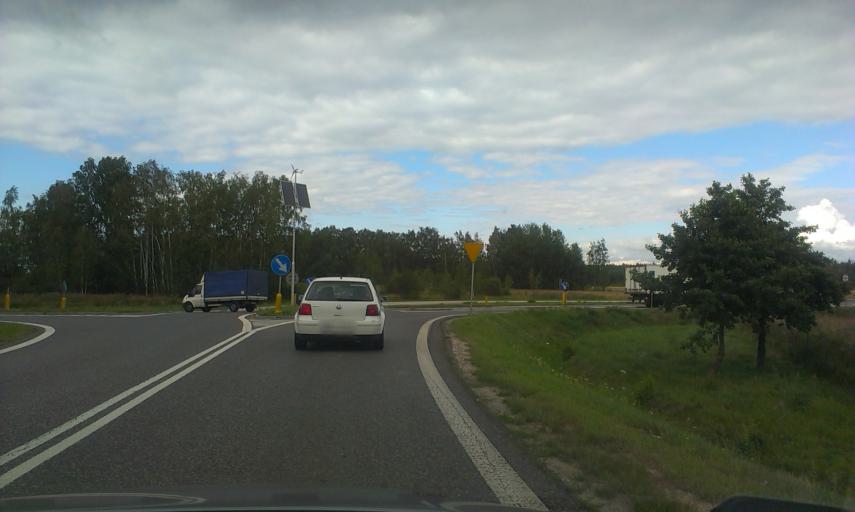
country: PL
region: Masovian Voivodeship
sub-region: Powiat zyrardowski
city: Mszczonow
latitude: 51.9930
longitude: 20.5024
